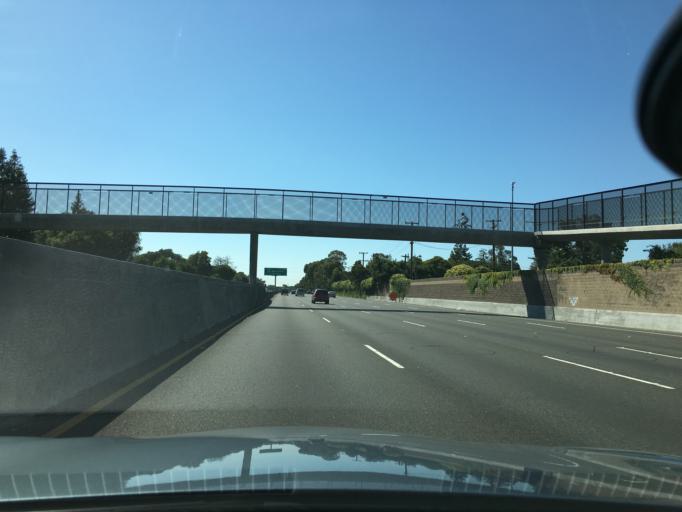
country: US
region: California
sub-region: San Mateo County
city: East Palo Alto
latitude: 37.4751
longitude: -122.1657
